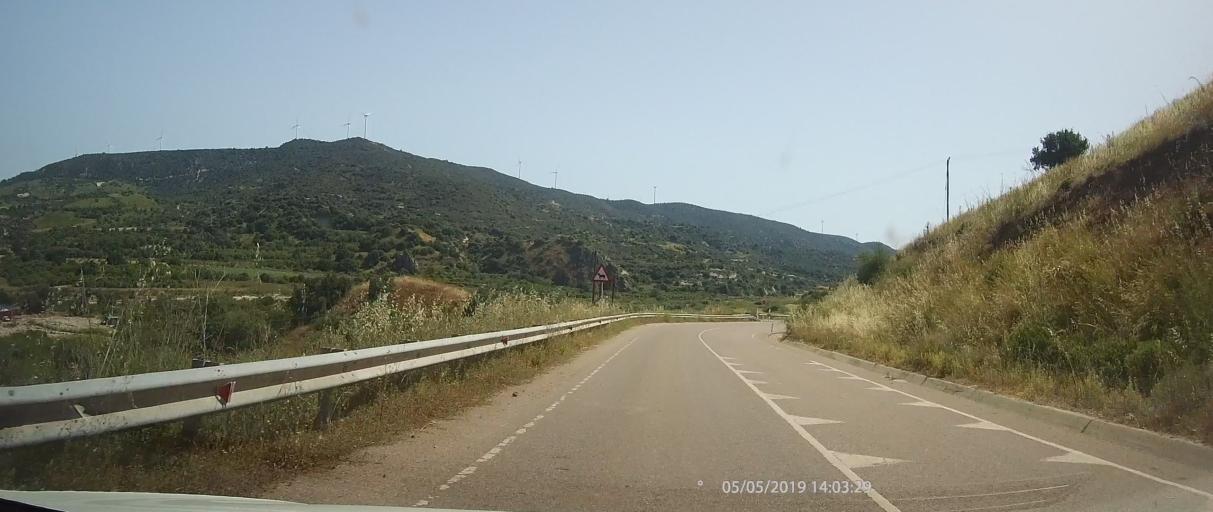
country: CY
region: Limassol
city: Pissouri
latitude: 34.7678
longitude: 32.6343
